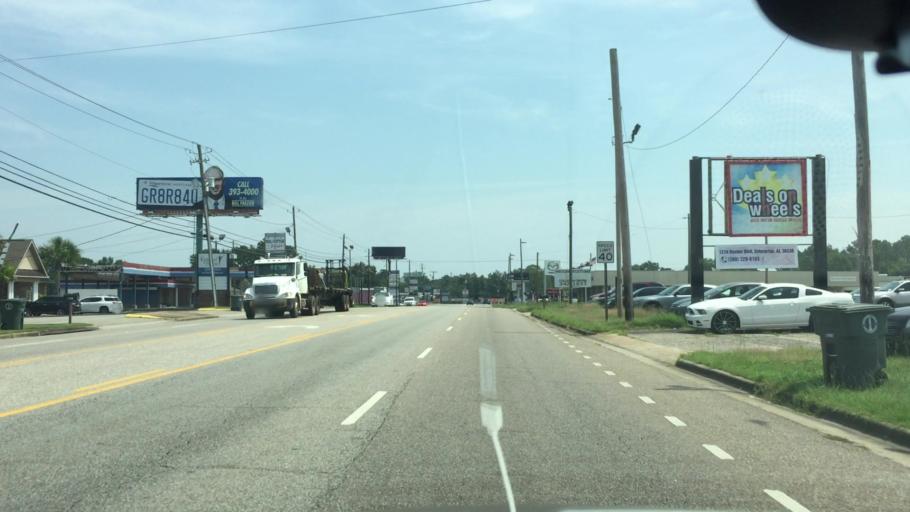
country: US
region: Alabama
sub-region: Coffee County
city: Enterprise
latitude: 31.3280
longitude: -85.8187
